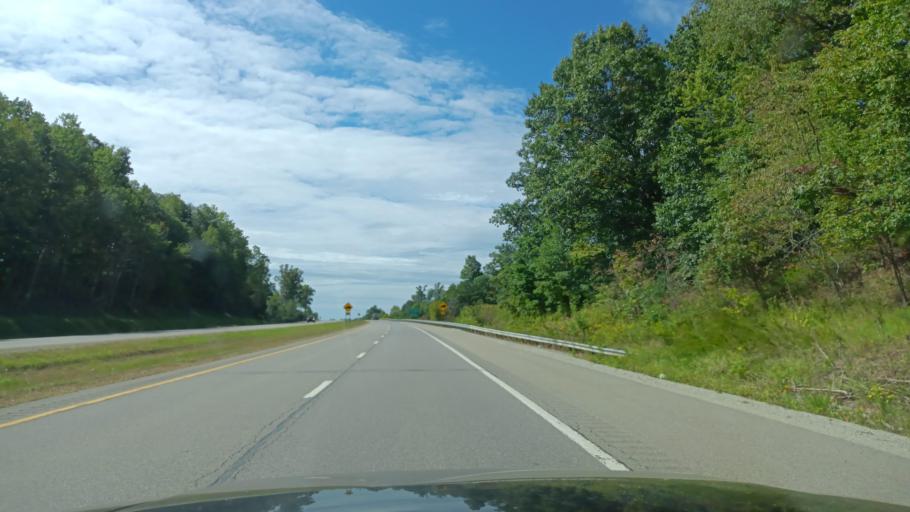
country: US
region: West Virginia
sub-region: Ritchie County
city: Pennsboro
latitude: 39.2744
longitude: -81.0162
